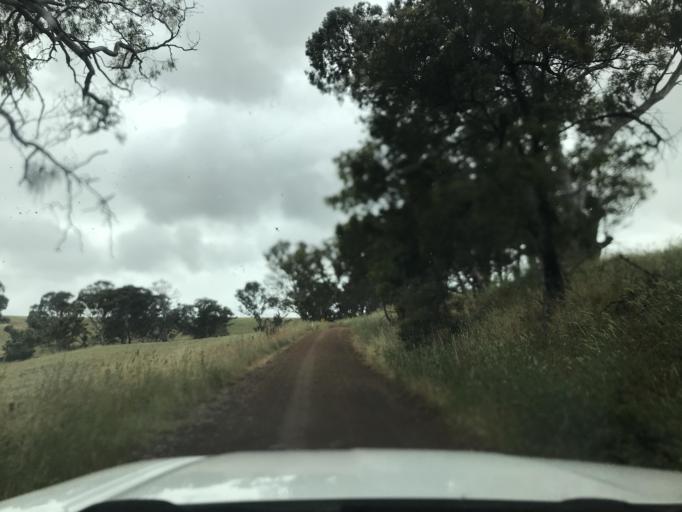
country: AU
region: South Australia
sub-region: Wattle Range
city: Penola
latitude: -37.2345
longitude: 141.4654
